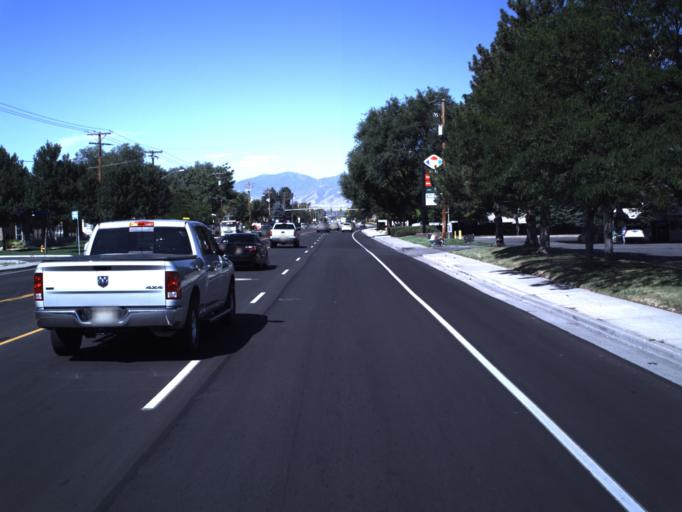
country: US
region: Utah
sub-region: Salt Lake County
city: Millcreek
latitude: 40.6744
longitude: -111.8672
